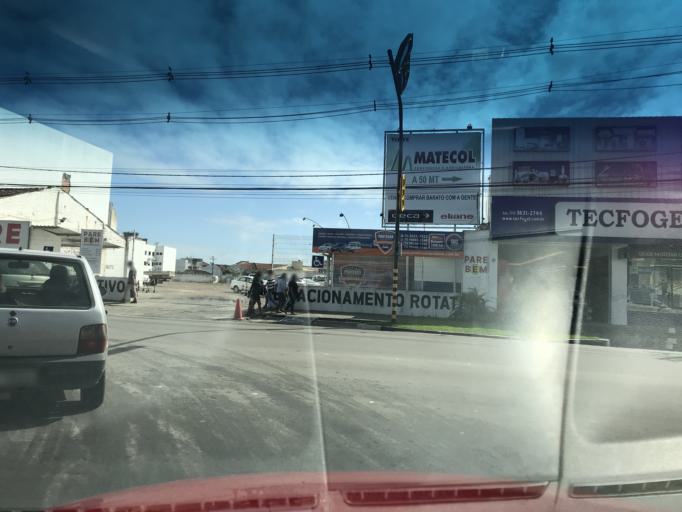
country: BR
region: Bahia
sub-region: Santo Antonio De Jesus
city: Santo Antonio de Jesus
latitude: -12.9662
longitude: -39.2632
